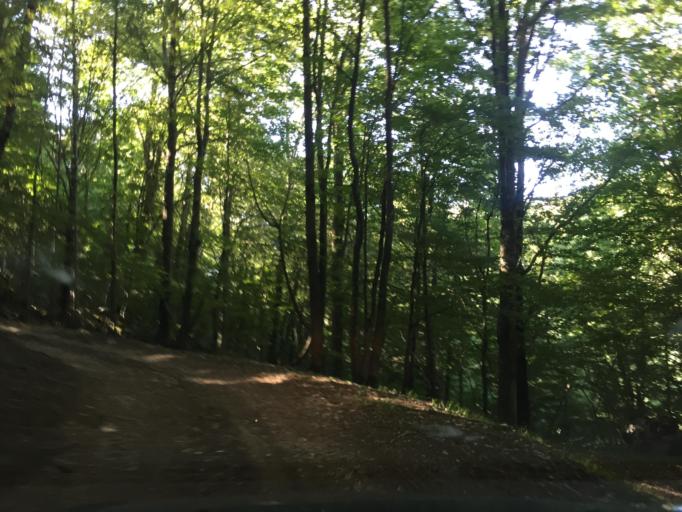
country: HR
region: Primorsko-Goranska
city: Klana
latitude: 45.4687
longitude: 14.4257
